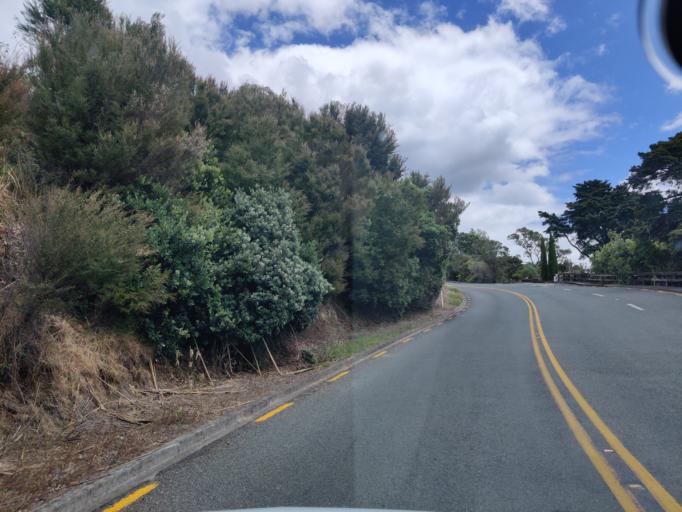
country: NZ
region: Northland
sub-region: Far North District
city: Paihia
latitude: -35.3135
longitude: 174.1200
